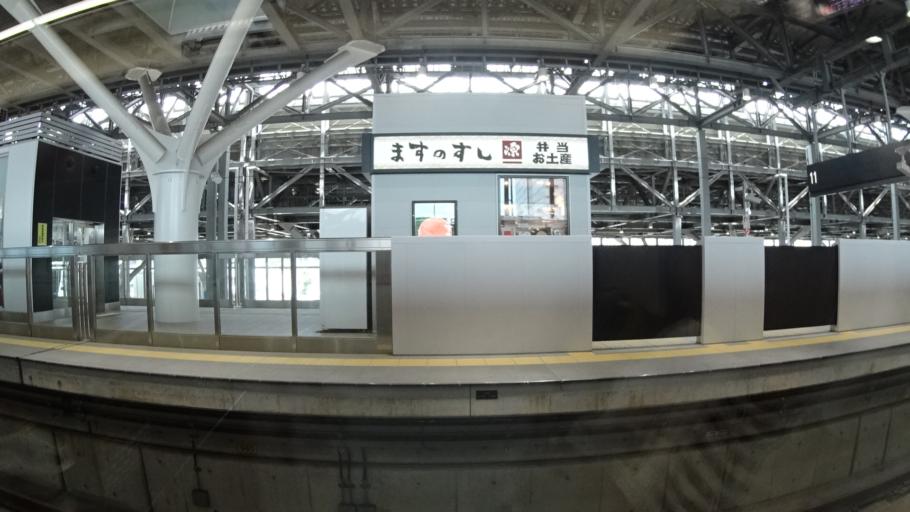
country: JP
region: Toyama
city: Toyama-shi
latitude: 36.7016
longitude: 137.2133
